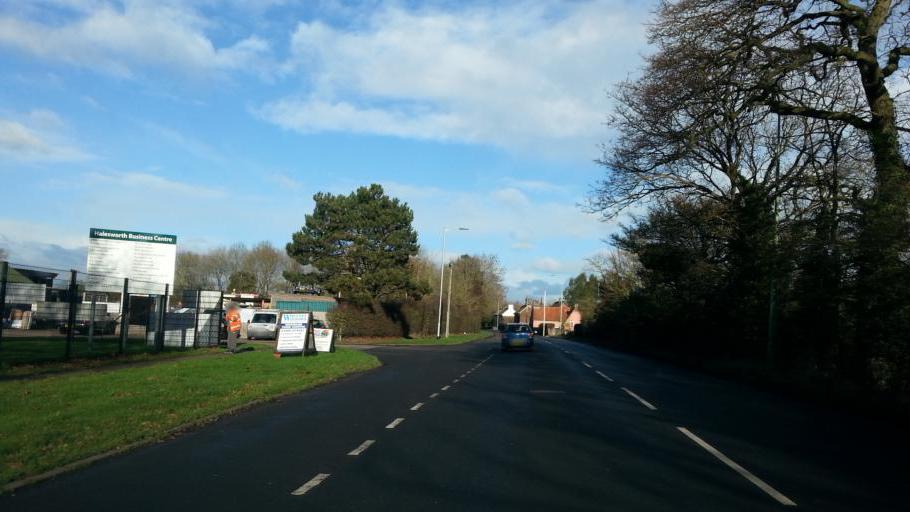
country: GB
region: England
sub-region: Suffolk
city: Halesworth
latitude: 52.3541
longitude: 1.5109
